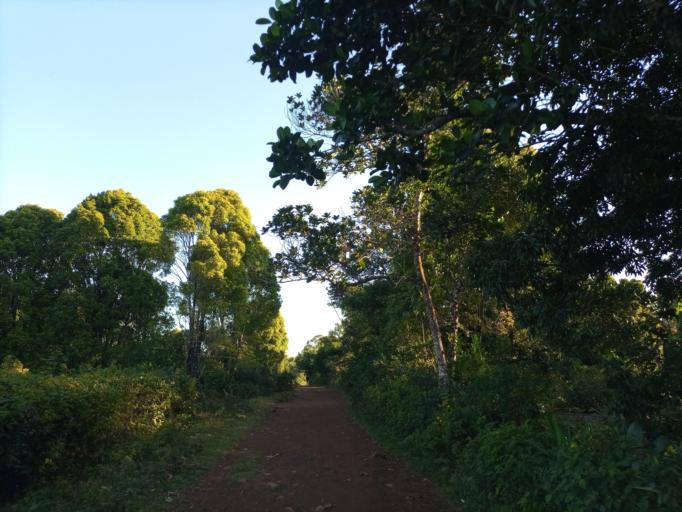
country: MG
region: Atsimo-Atsinanana
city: Vohipaho
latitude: -23.5242
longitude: 47.6202
